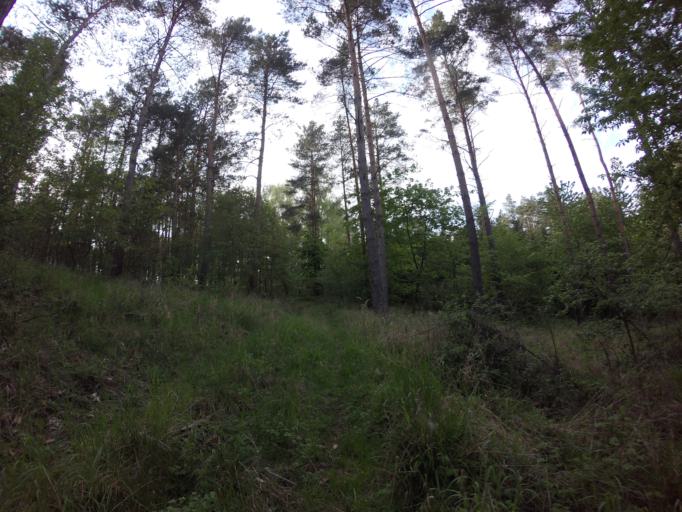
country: PL
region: West Pomeranian Voivodeship
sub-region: Powiat choszczenski
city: Choszczno
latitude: 53.1475
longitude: 15.3423
